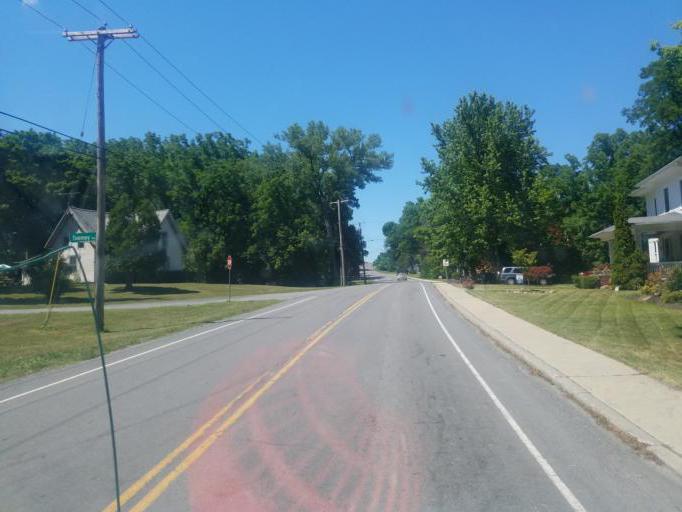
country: US
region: New York
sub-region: Yates County
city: Penn Yan
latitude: 42.7581
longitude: -77.0153
